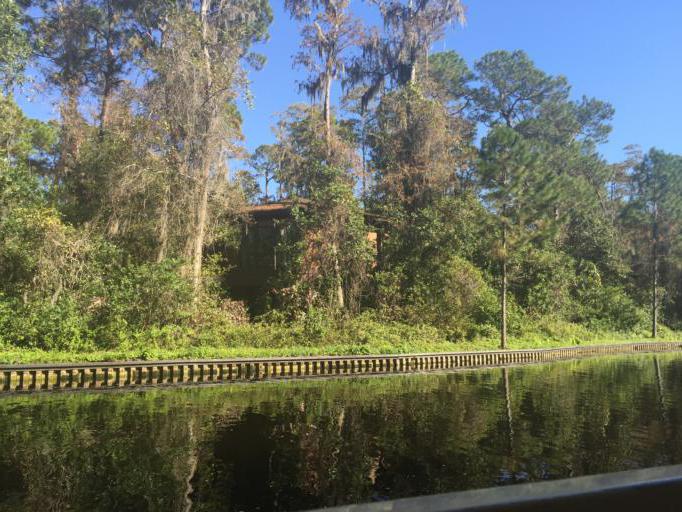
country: US
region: Florida
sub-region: Osceola County
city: Celebration
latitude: 28.3778
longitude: -81.5298
